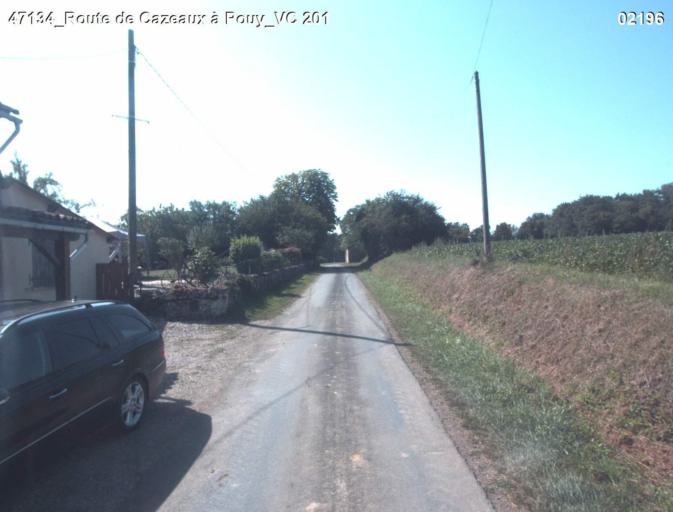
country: FR
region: Aquitaine
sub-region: Departement du Lot-et-Garonne
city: Mezin
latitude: 44.0204
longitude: 0.3133
